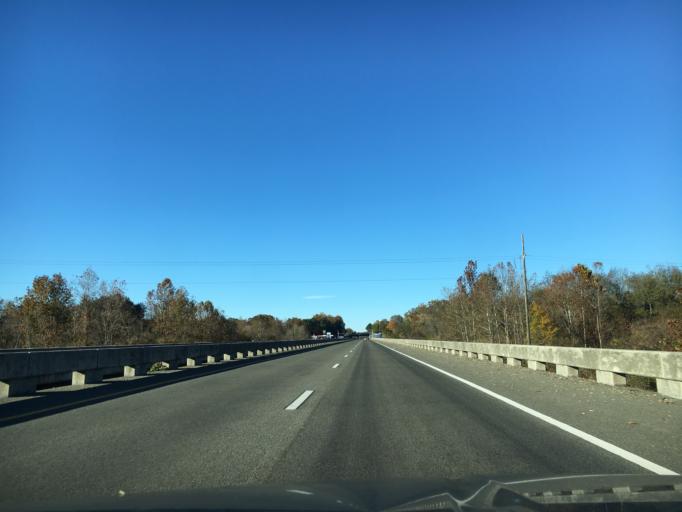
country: US
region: Virginia
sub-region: Halifax County
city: South Boston
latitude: 36.6927
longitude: -78.8875
